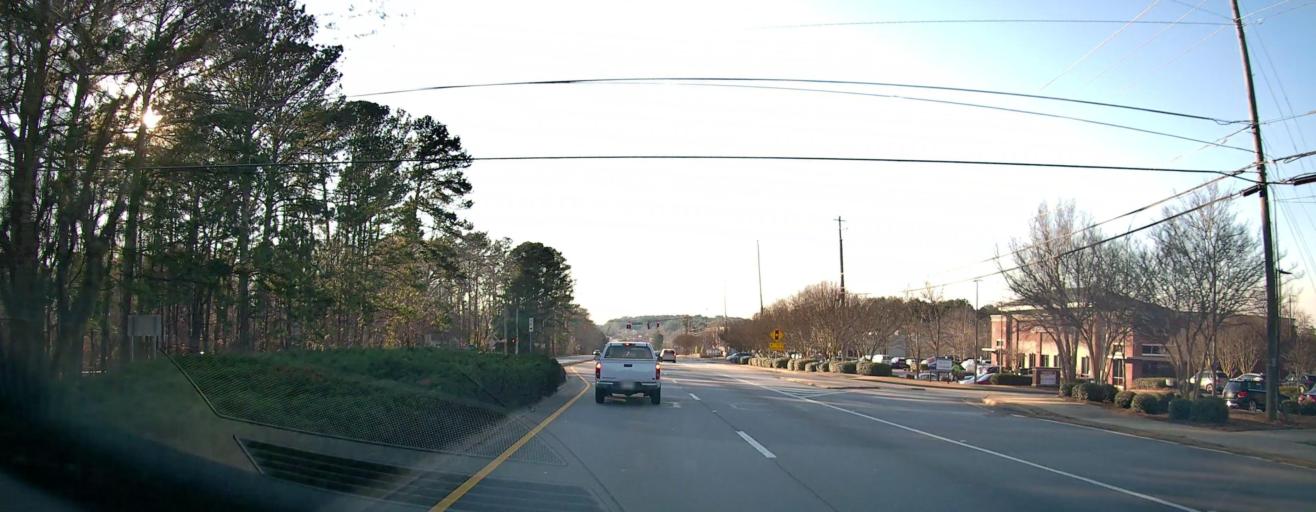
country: US
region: Georgia
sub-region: Fayette County
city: Fayetteville
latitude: 33.4472
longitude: -84.4731
